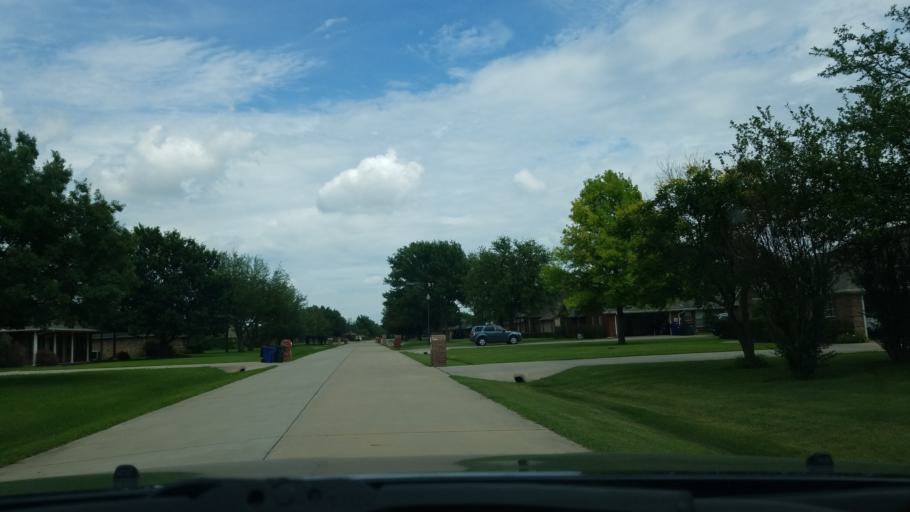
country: US
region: Texas
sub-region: Denton County
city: Sanger
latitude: 33.3598
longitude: -97.1978
